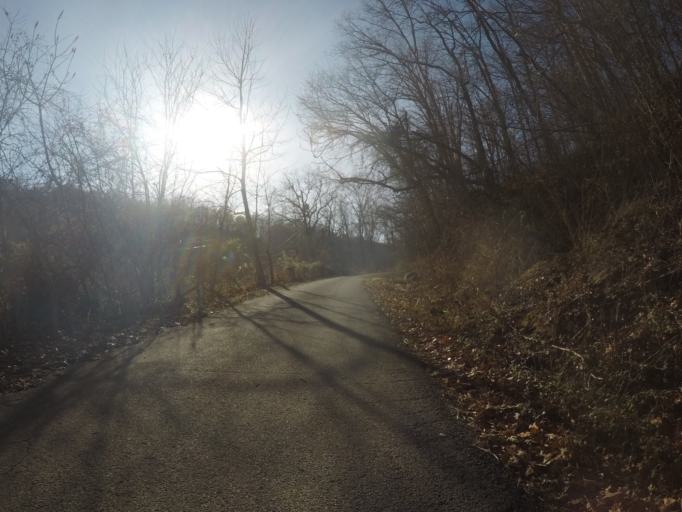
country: US
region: Ohio
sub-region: Lawrence County
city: Burlington
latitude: 38.3908
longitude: -82.4893
